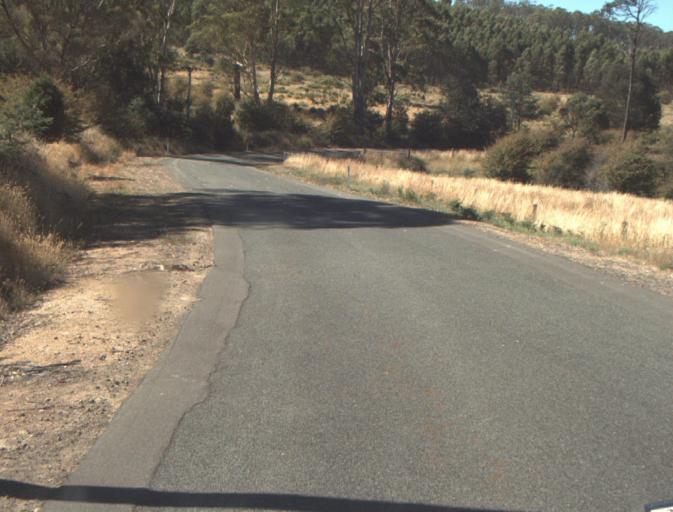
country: AU
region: Tasmania
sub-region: Launceston
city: Newstead
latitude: -41.3479
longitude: 147.3036
